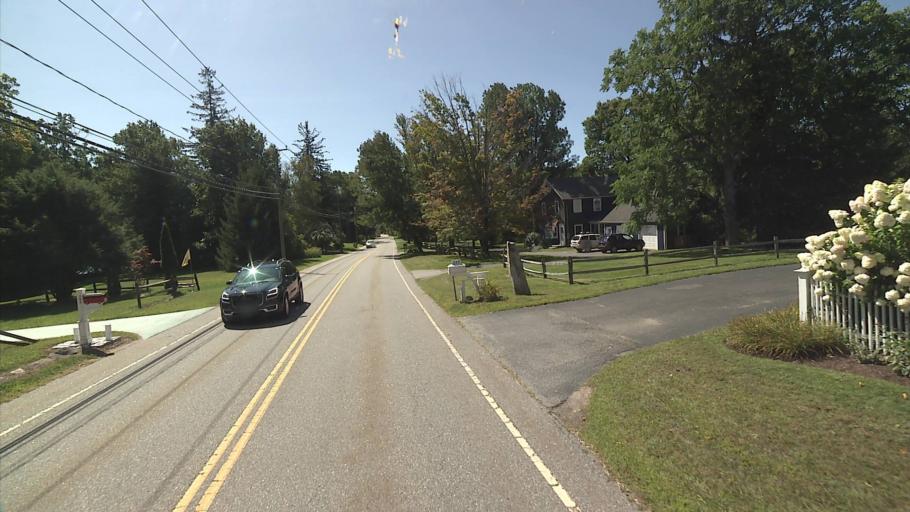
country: US
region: Connecticut
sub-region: Litchfield County
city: Litchfield
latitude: 41.7015
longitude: -73.2332
